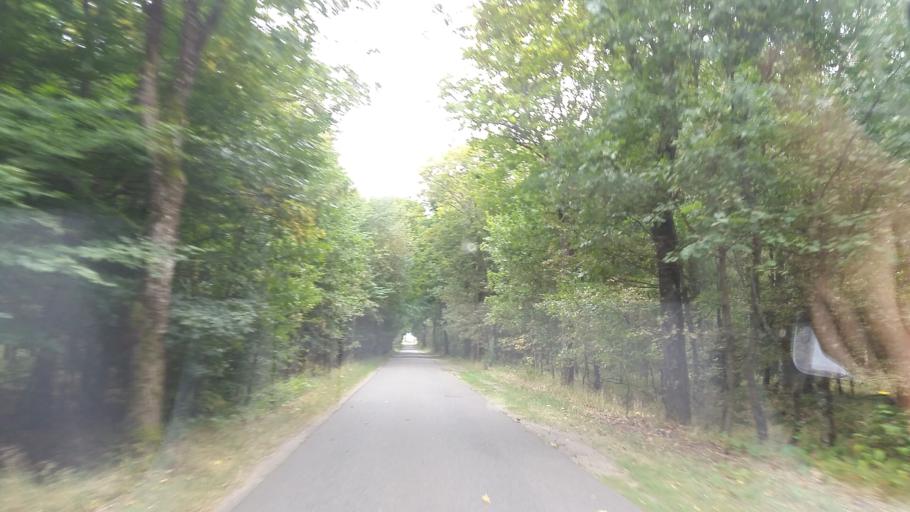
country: PL
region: West Pomeranian Voivodeship
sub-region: Powiat choszczenski
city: Bierzwnik
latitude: 52.9853
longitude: 15.5834
